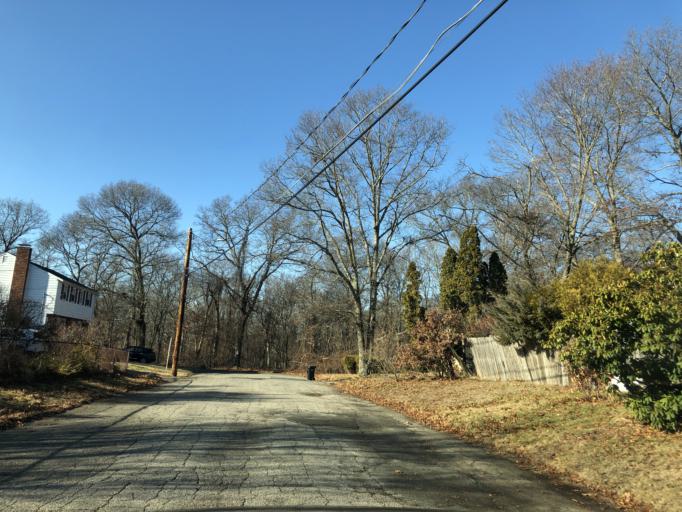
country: US
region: Massachusetts
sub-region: Plymouth County
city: Brockton
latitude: 42.0985
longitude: -71.0024
